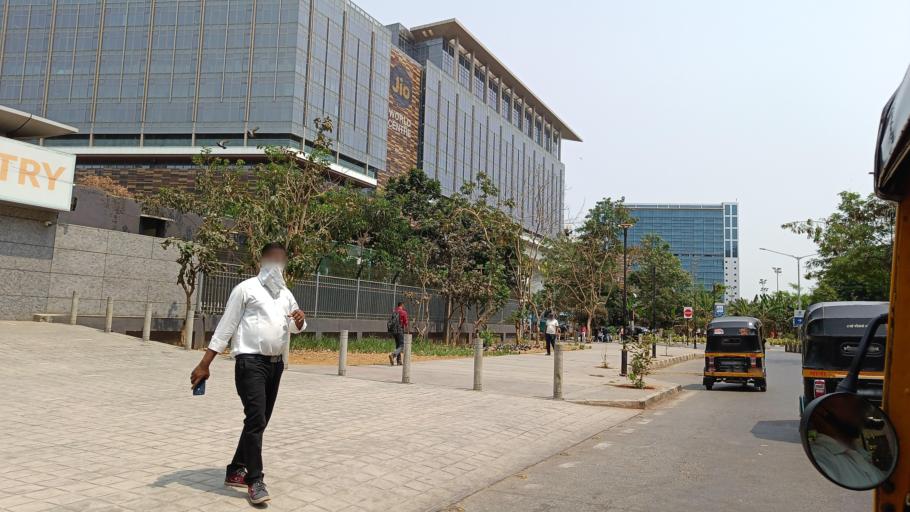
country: IN
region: Maharashtra
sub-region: Mumbai Suburban
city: Mumbai
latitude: 19.0633
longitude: 72.8645
